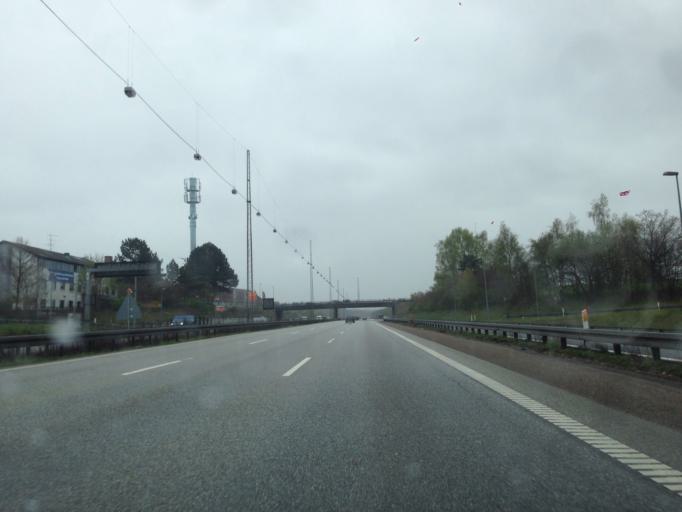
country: DK
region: Capital Region
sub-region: Rudersdal Kommune
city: Trorod
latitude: 55.8170
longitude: 12.5273
